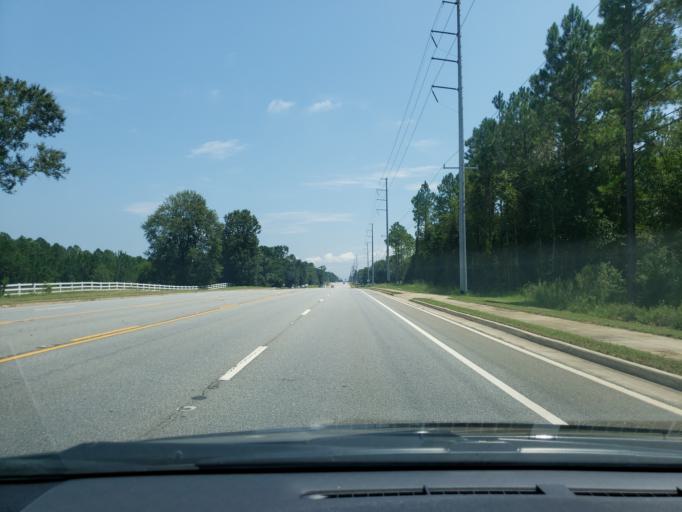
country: US
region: Georgia
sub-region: Dougherty County
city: Albany
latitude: 31.5856
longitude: -84.2608
